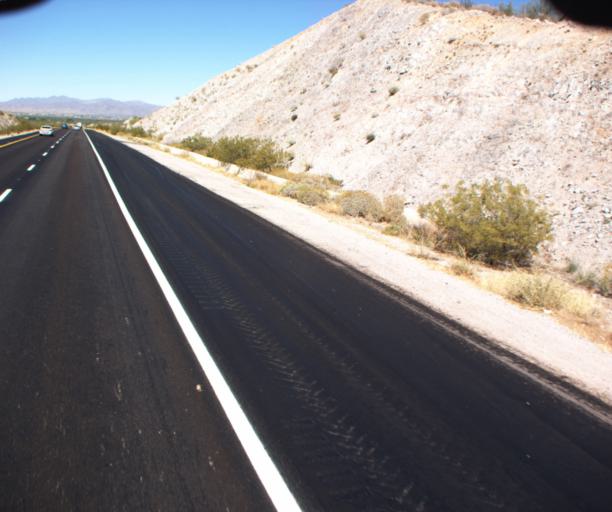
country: US
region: Arizona
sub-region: Maricopa County
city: Buckeye
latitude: 33.2996
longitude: -112.6269
